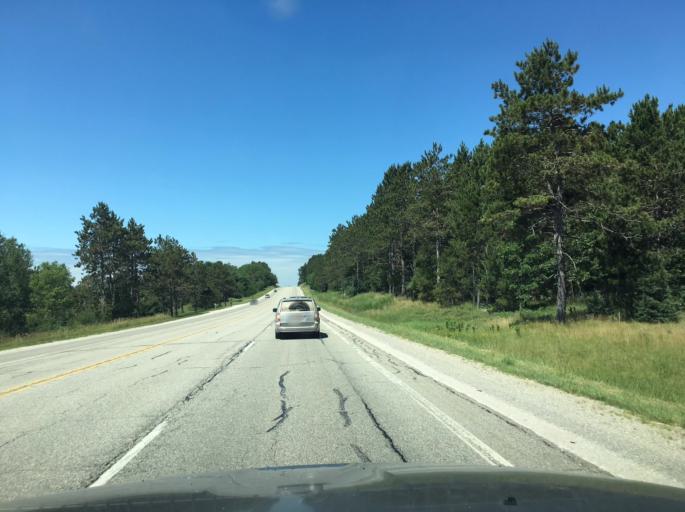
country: US
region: Michigan
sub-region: Osceola County
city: Reed City
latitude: 43.8879
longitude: -85.6075
